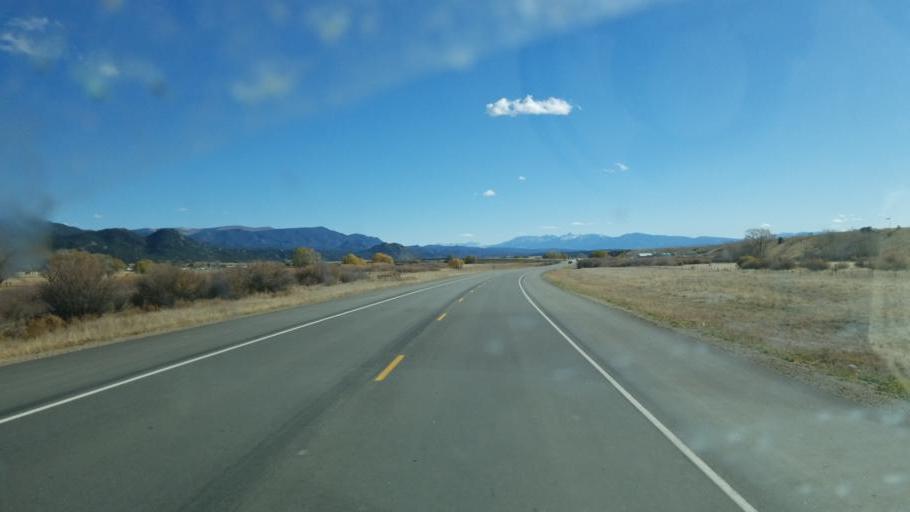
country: US
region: Colorado
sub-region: Chaffee County
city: Buena Vista
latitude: 38.8194
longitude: -106.1201
